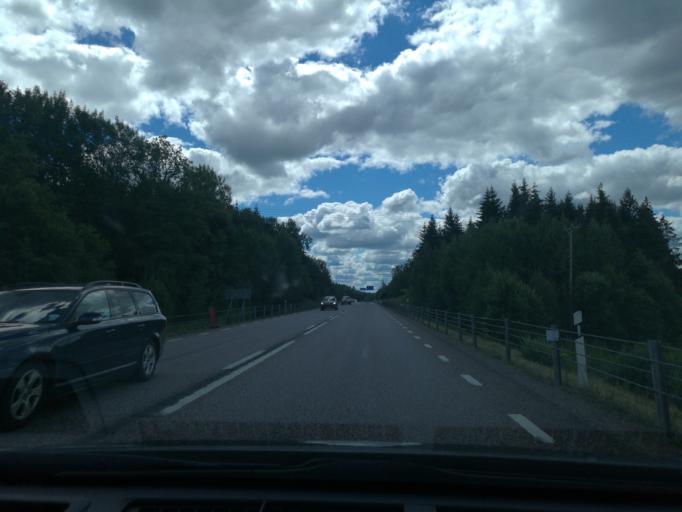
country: SE
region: Soedermanland
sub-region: Eskilstuna Kommun
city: Kvicksund
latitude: 59.4981
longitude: 16.3038
